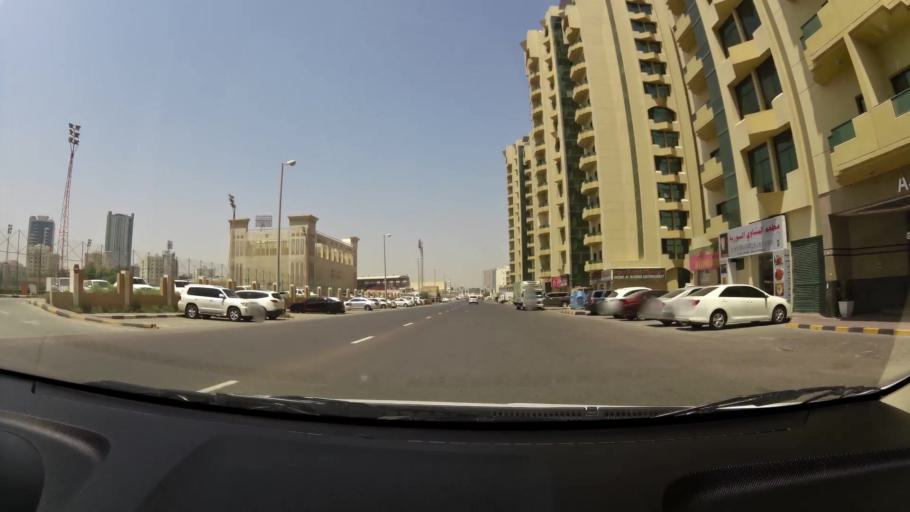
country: AE
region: Ajman
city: Ajman
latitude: 25.3947
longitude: 55.4521
